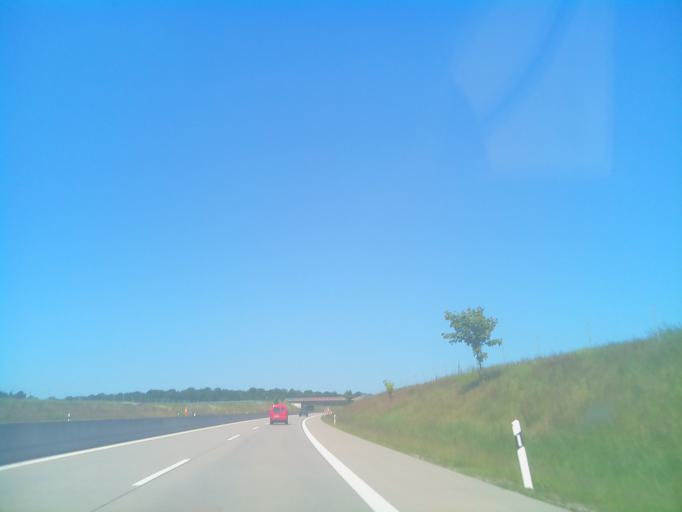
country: DE
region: Bavaria
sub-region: Regierungsbezirk Unterfranken
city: Strahlungen
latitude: 50.2884
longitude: 10.2629
